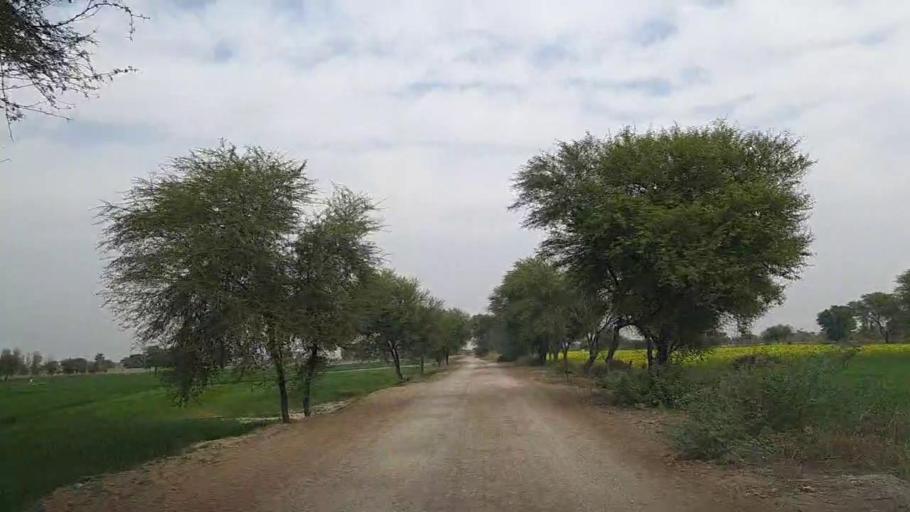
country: PK
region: Sindh
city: Daur
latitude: 26.4307
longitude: 68.4638
